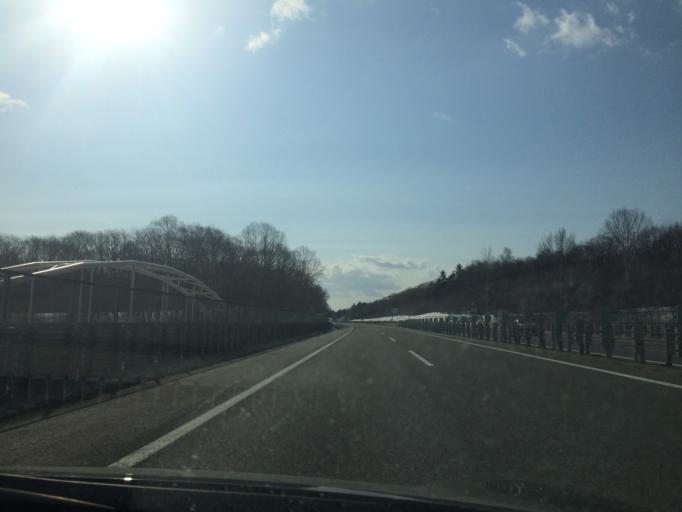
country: JP
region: Hokkaido
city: Chitose
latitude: 42.8623
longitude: 141.5587
